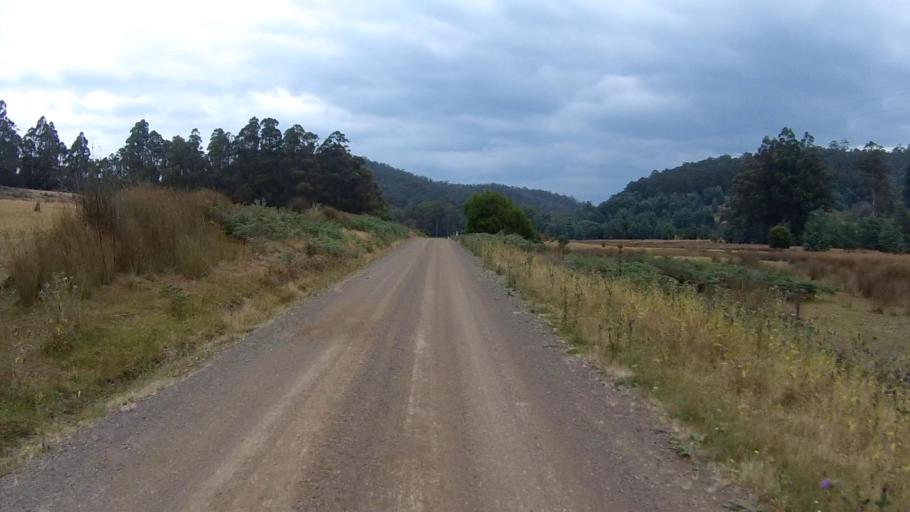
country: AU
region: Tasmania
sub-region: Kingborough
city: Kettering
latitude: -43.2171
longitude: 147.1769
